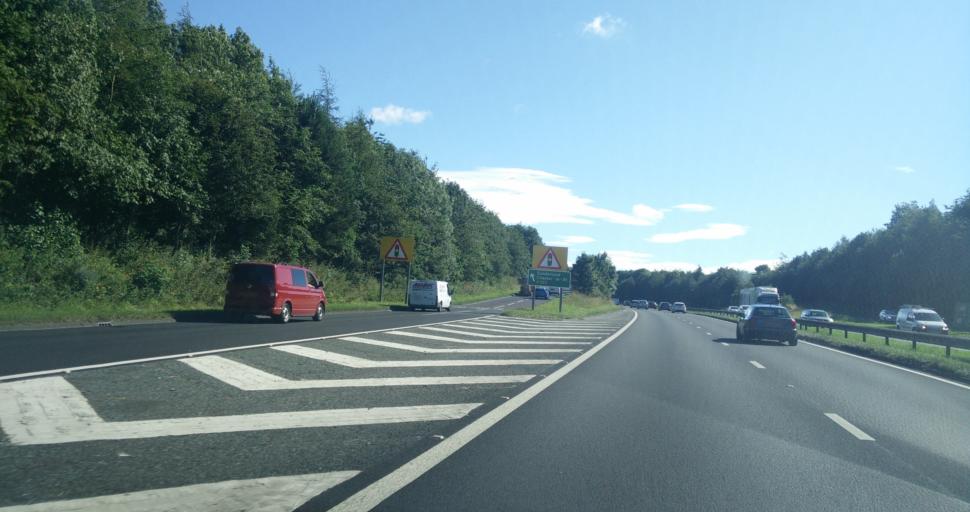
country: GB
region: England
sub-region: South Tyneside
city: The Boldons
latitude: 54.8939
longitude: -1.4572
